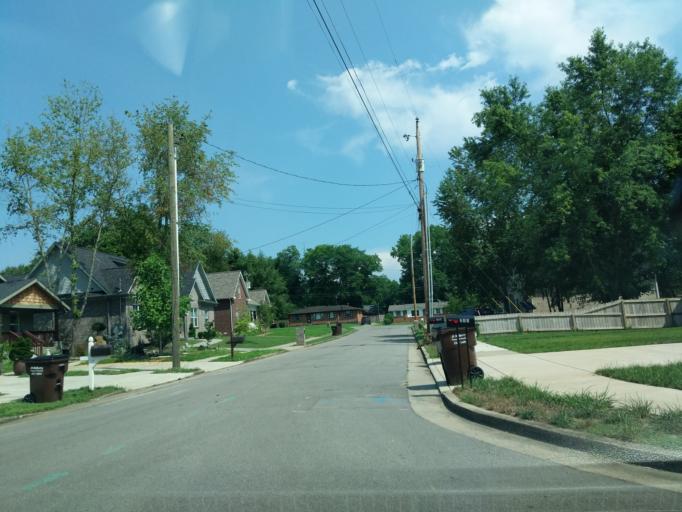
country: US
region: Tennessee
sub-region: Davidson County
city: Lakewood
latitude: 36.2810
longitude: -86.6762
